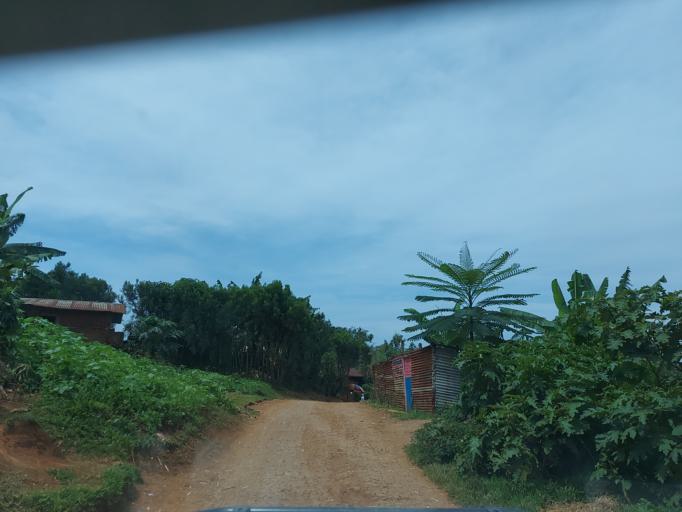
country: CD
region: South Kivu
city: Bukavu
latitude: -2.2367
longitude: 28.8464
